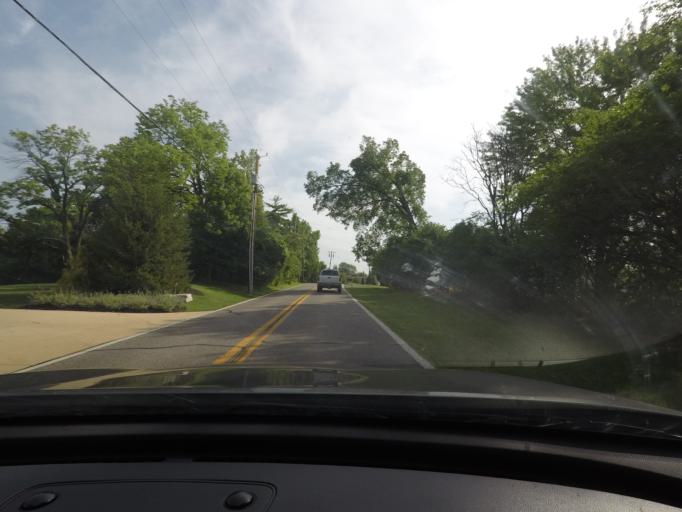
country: US
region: Missouri
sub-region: Saint Louis County
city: Town and Country
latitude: 38.6193
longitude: -90.4851
